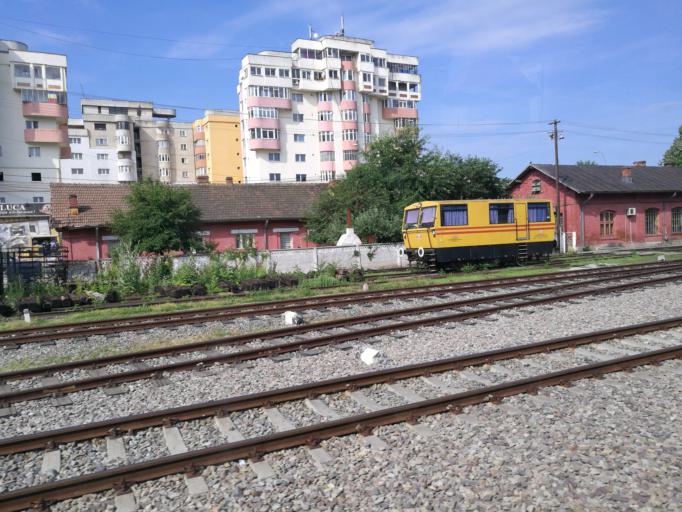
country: RO
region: Arges
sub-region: Comuna Bradu
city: Geamana
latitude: 44.8452
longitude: 24.8915
